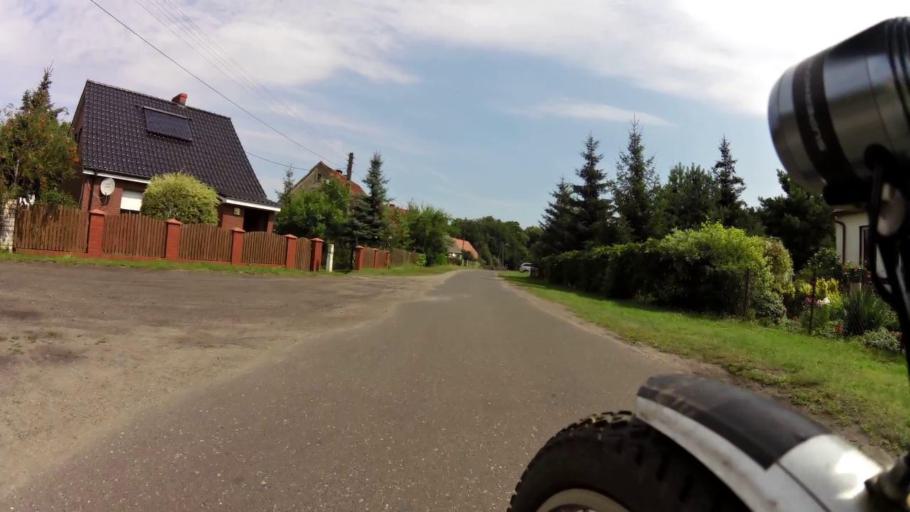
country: PL
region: West Pomeranian Voivodeship
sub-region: Powiat mysliborski
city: Boleszkowice
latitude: 52.6772
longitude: 14.5950
